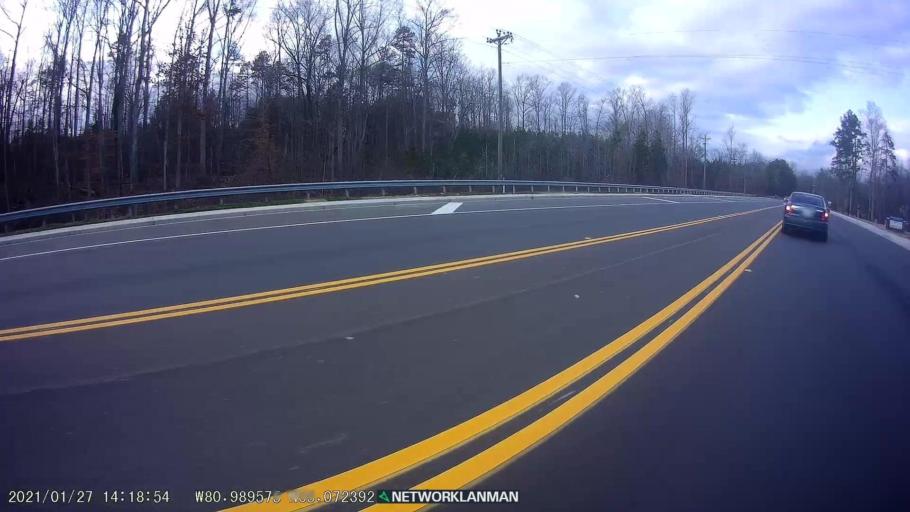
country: US
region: South Carolina
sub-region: York County
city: Tega Cay
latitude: 35.0725
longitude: -80.9894
